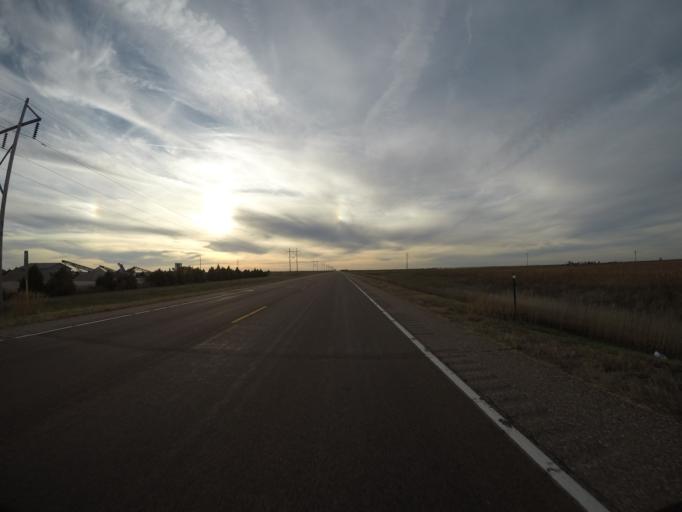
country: US
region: Colorado
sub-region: Yuma County
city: Yuma
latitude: 39.6559
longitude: -102.7148
